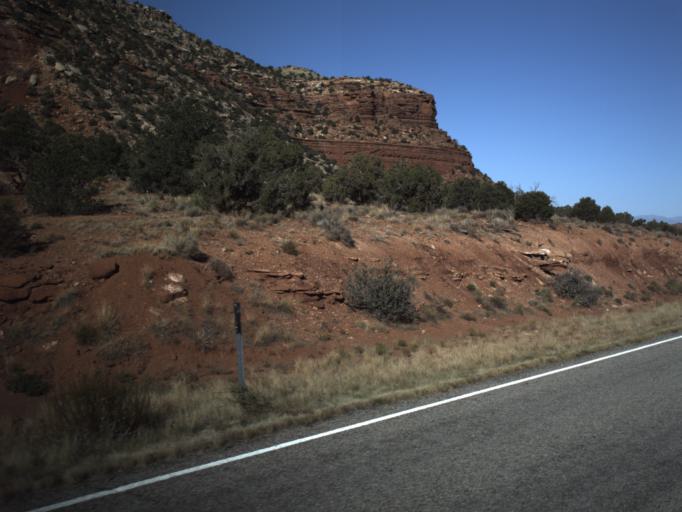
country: US
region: Utah
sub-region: San Juan County
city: Blanding
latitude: 37.6456
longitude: -110.1135
